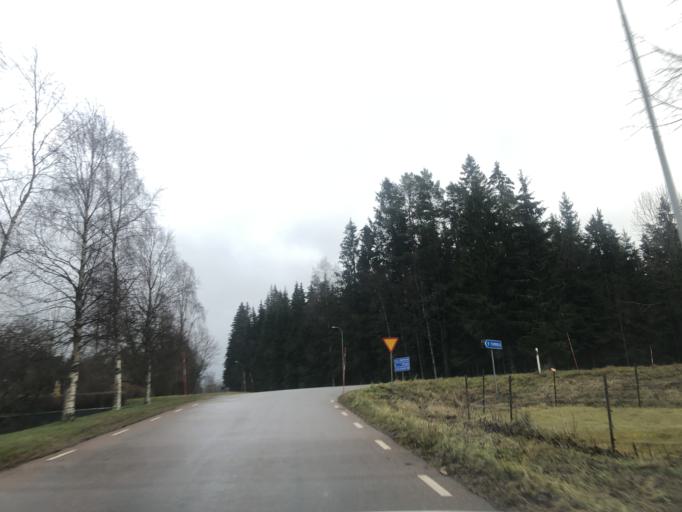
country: SE
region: Vaestra Goetaland
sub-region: Ulricehamns Kommun
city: Ulricehamn
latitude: 57.8251
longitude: 13.5160
